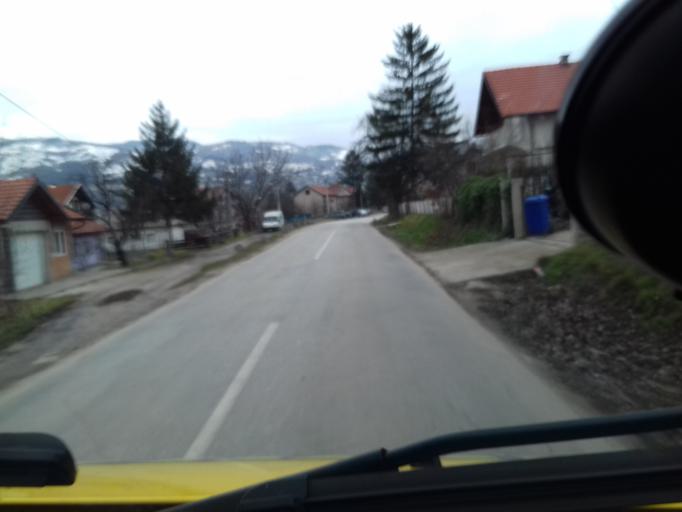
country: BA
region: Federation of Bosnia and Herzegovina
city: Zenica
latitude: 44.1846
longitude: 17.9521
